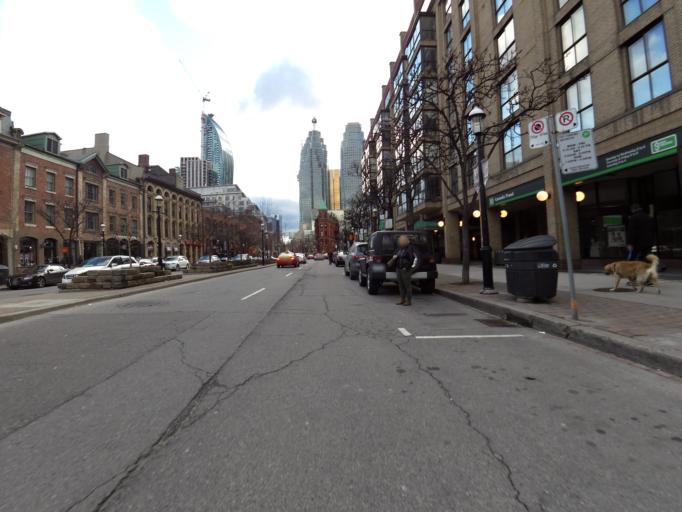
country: CA
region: Ontario
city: Toronto
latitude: 43.6491
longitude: -79.3722
